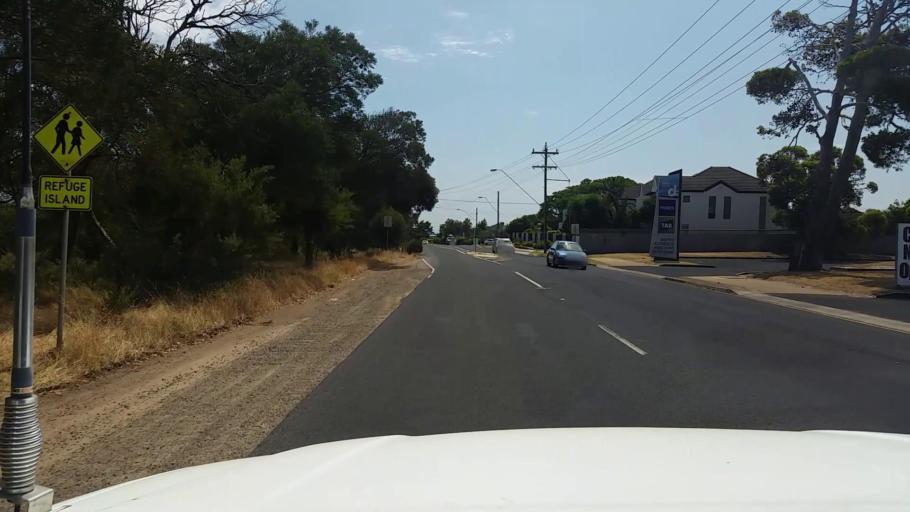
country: AU
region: Victoria
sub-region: Mornington Peninsula
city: Mount Martha
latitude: -38.2447
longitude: 145.0298
